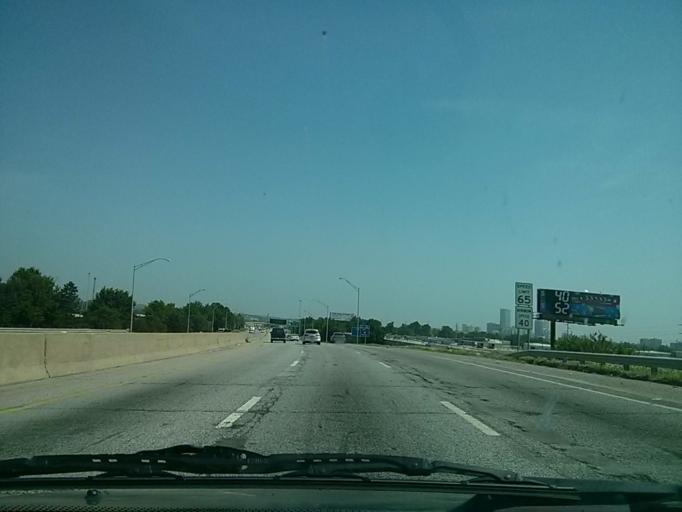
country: US
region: Oklahoma
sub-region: Tulsa County
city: Tulsa
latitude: 36.1188
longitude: -96.0087
